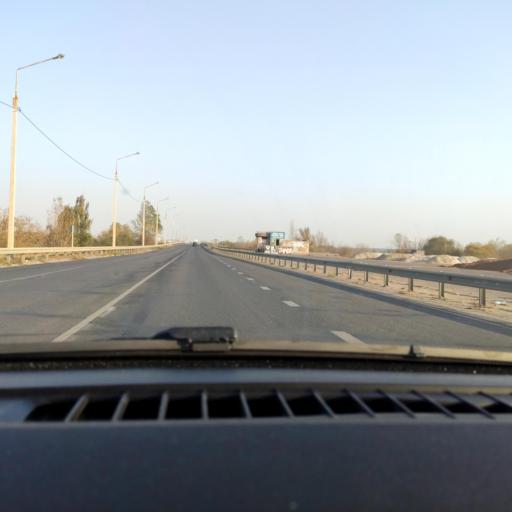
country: RU
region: Voronezj
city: Pridonskoy
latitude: 51.7251
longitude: 39.0571
